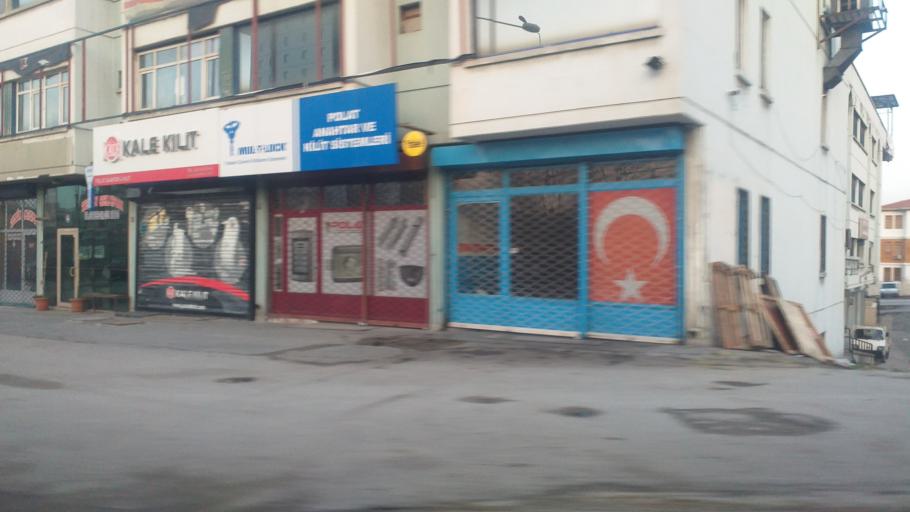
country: TR
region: Ankara
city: Ankara
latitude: 39.9525
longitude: 32.8551
